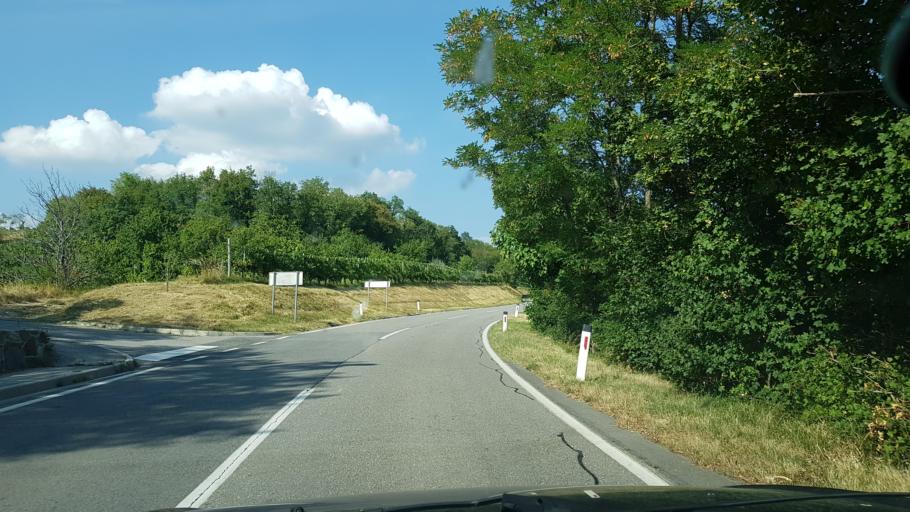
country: SI
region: Brda
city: Dobrovo
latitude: 46.0070
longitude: 13.5569
